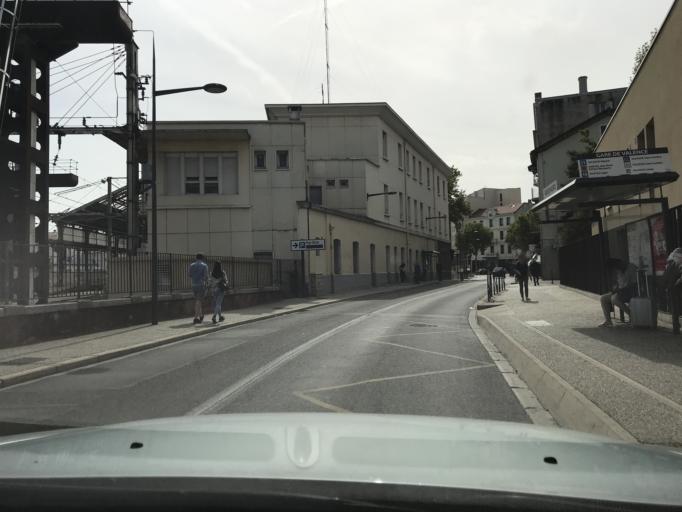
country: FR
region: Rhone-Alpes
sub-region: Departement de la Drome
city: Valence
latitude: 44.9291
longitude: 4.8939
